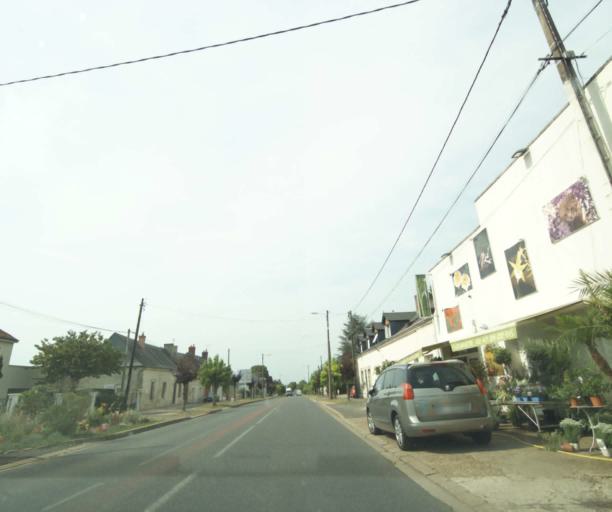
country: FR
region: Centre
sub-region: Departement d'Indre-et-Loire
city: Neuille-Pont-Pierre
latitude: 47.5483
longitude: 0.5511
